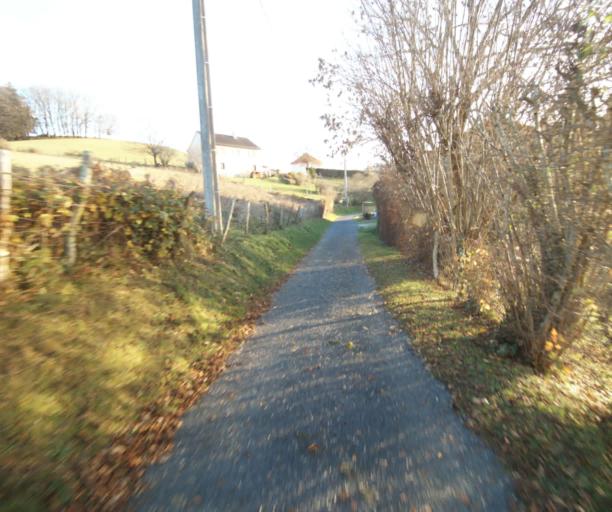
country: FR
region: Limousin
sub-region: Departement de la Correze
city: Laguenne
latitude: 45.2449
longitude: 1.8180
